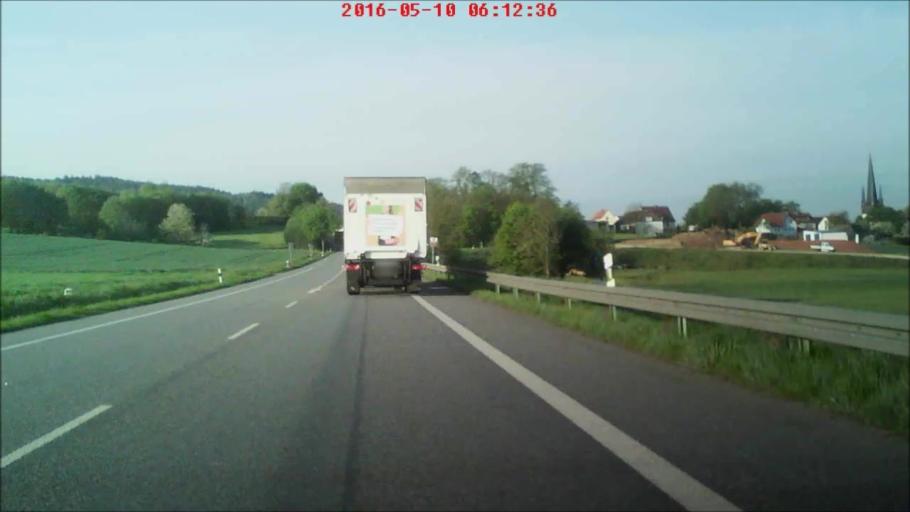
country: DE
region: Hesse
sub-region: Regierungsbezirk Kassel
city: Burghaun
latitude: 50.7756
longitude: 9.7022
